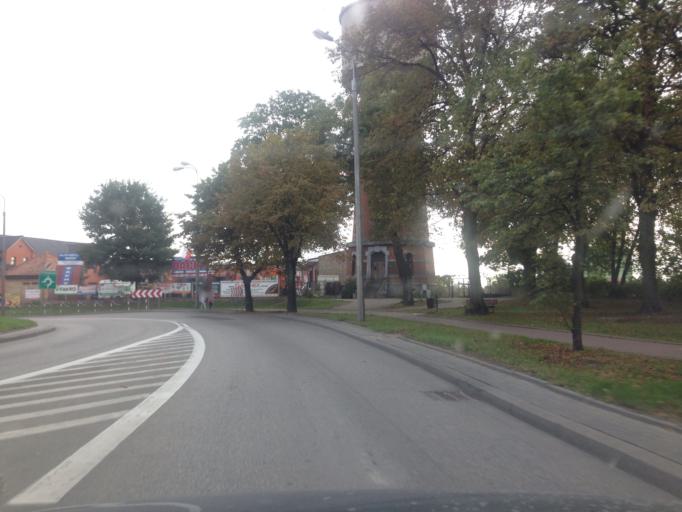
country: PL
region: Pomeranian Voivodeship
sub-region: Powiat kwidzynski
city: Kwidzyn
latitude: 53.7239
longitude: 18.9315
